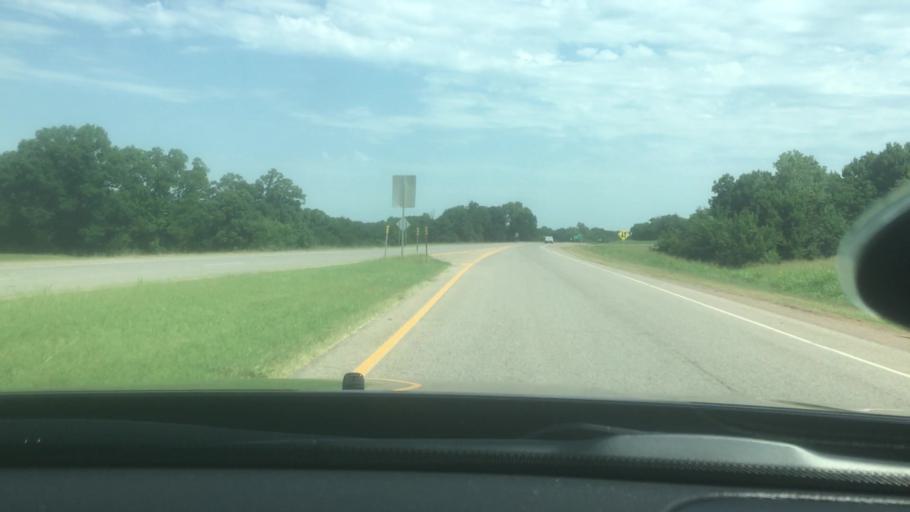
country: US
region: Oklahoma
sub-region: Seminole County
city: Konawa
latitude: 34.9881
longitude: -96.9304
